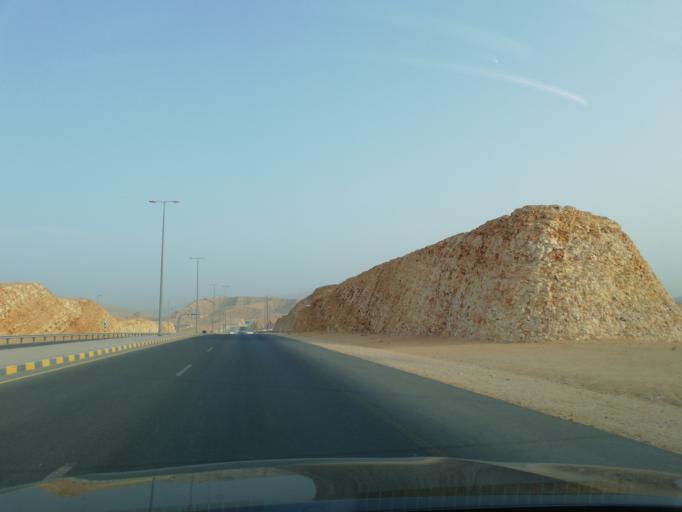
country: OM
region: Muhafazat Masqat
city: Bawshar
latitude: 23.5551
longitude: 58.2911
